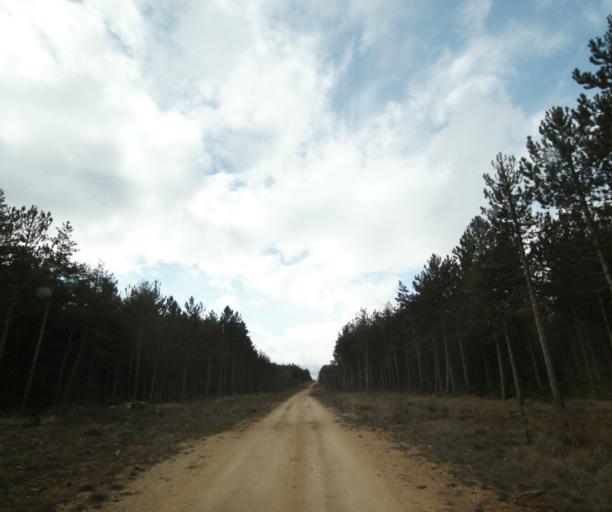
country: FR
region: Midi-Pyrenees
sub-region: Departement de l'Aveyron
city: Millau
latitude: 44.1274
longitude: 3.1527
